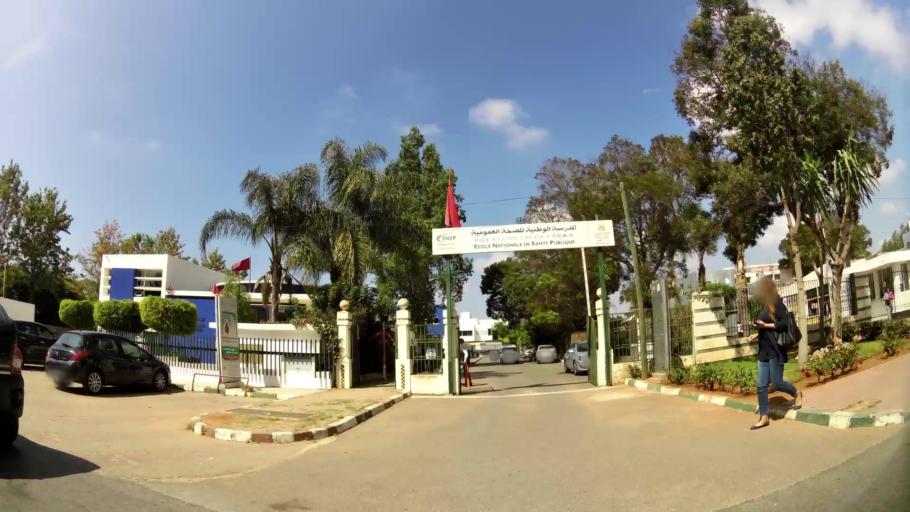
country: MA
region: Rabat-Sale-Zemmour-Zaer
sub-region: Rabat
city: Rabat
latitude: 33.9868
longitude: -6.8587
